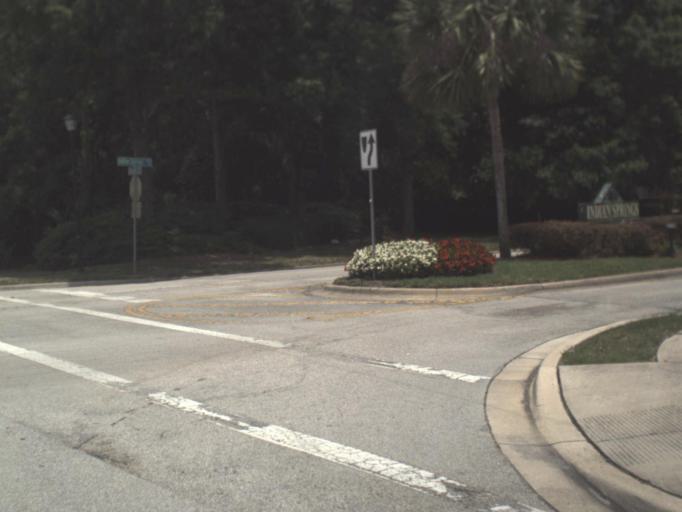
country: US
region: Florida
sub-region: Duval County
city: Atlantic Beach
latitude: 30.3192
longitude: -81.4701
